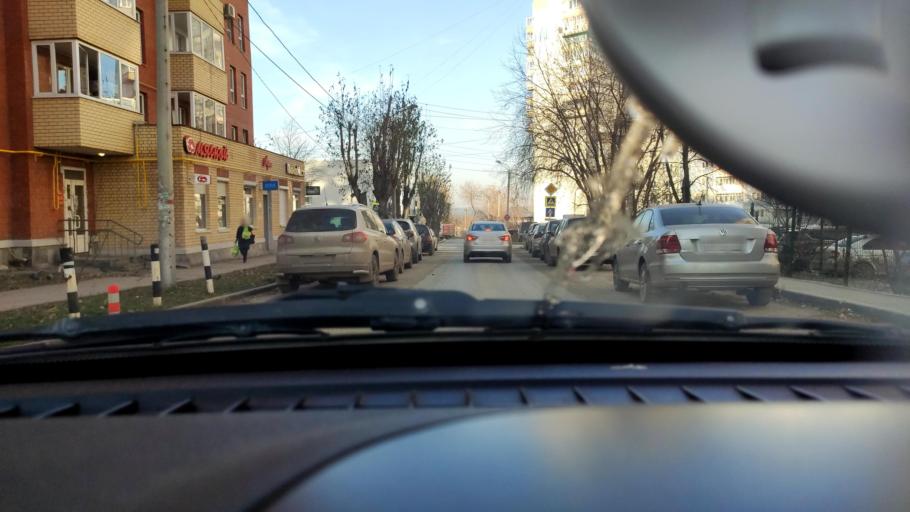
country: RU
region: Perm
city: Perm
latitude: 58.0295
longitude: 56.3050
